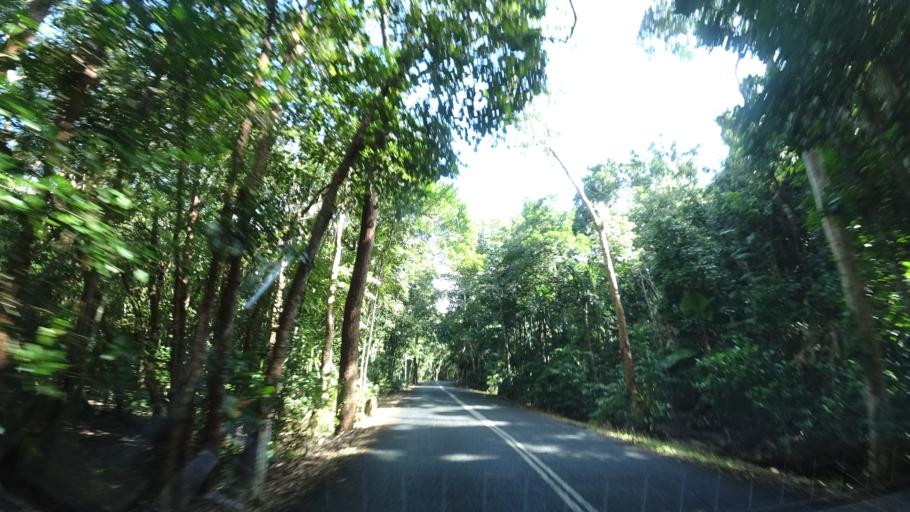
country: AU
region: Queensland
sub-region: Cairns
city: Port Douglas
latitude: -16.1397
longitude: 145.4443
